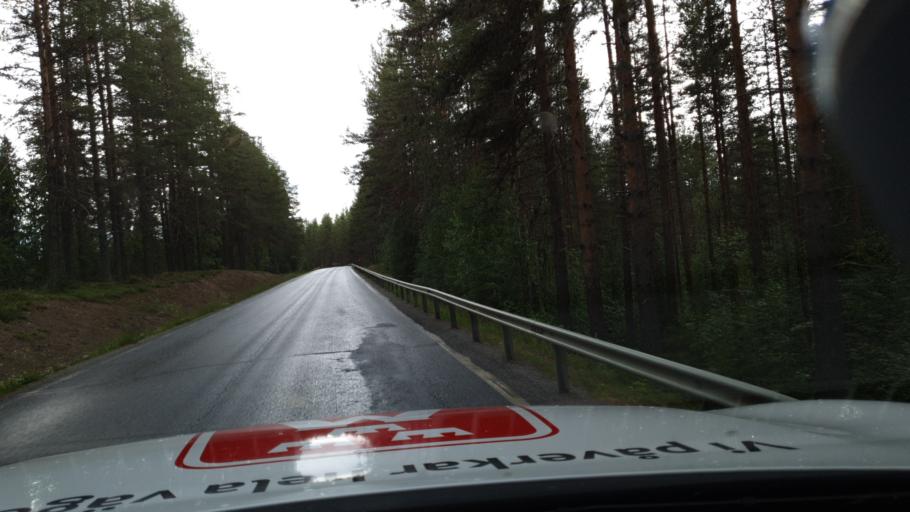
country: SE
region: Vaesterbotten
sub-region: Dorotea Kommun
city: Dorotea
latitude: 63.9054
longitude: 16.3554
